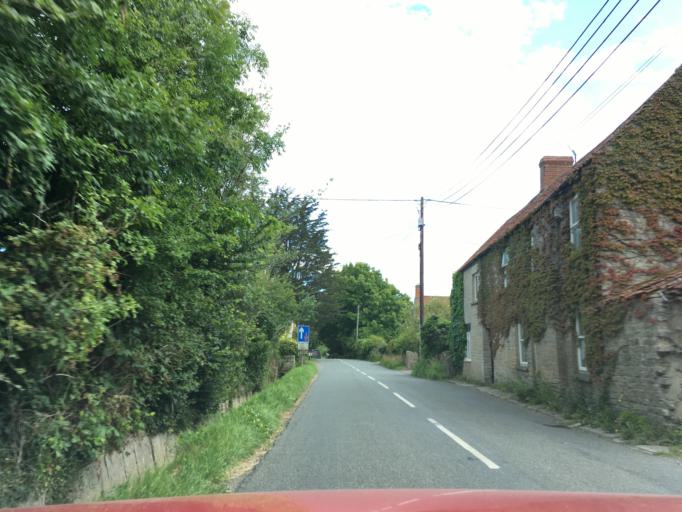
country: GB
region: England
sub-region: Somerset
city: Ilchester
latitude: 51.0578
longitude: -2.6715
